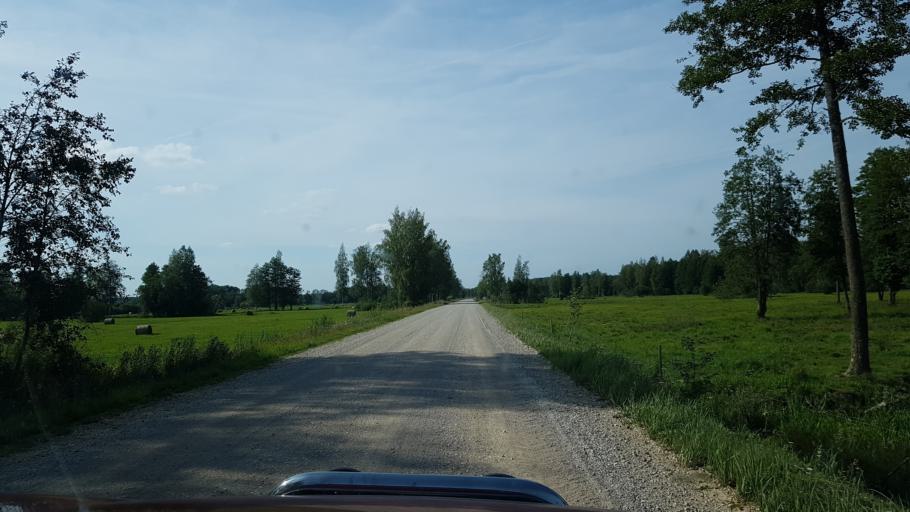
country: EE
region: Paernumaa
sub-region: Saarde vald
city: Kilingi-Nomme
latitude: 58.3616
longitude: 25.0782
